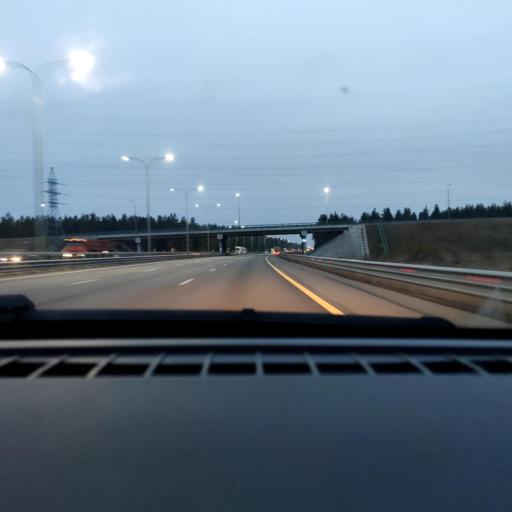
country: RU
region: Voronezj
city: Somovo
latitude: 51.7283
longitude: 39.3111
